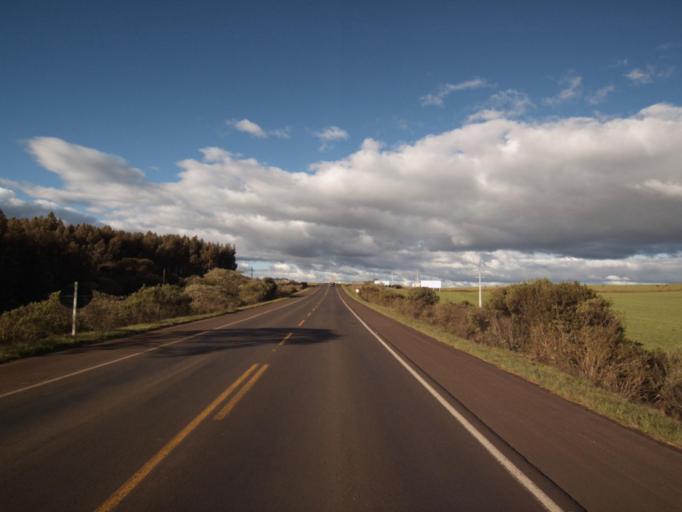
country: BR
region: Santa Catarina
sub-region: Campos Novos
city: Campos Novos
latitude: -27.3628
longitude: -51.3072
